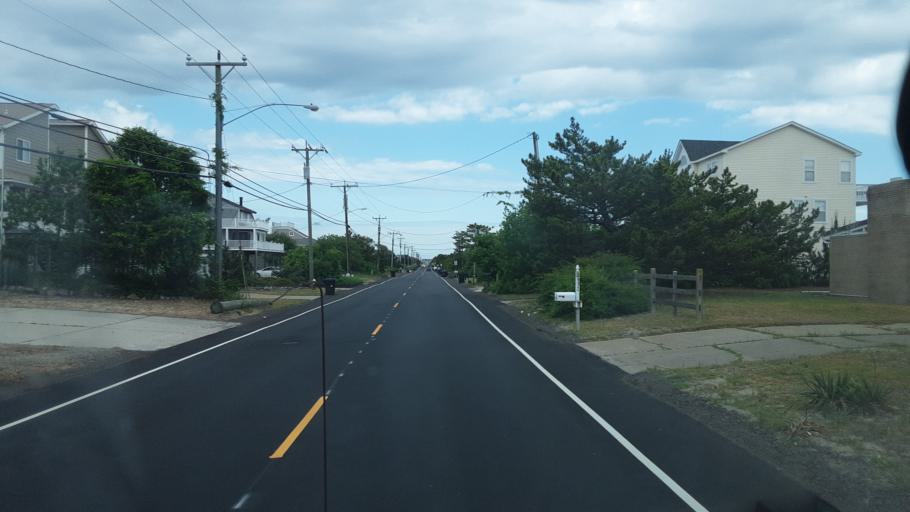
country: US
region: Virginia
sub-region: City of Virginia Beach
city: Virginia Beach
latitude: 36.7266
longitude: -75.9379
